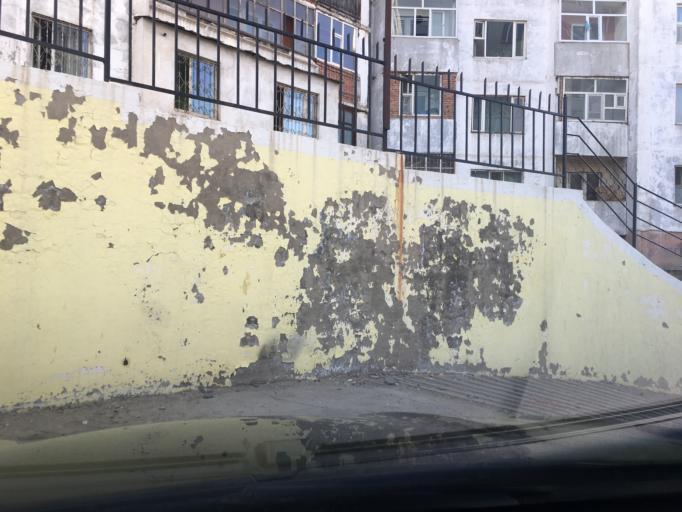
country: MN
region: Ulaanbaatar
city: Ulaanbaatar
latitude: 47.9284
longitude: 106.8814
